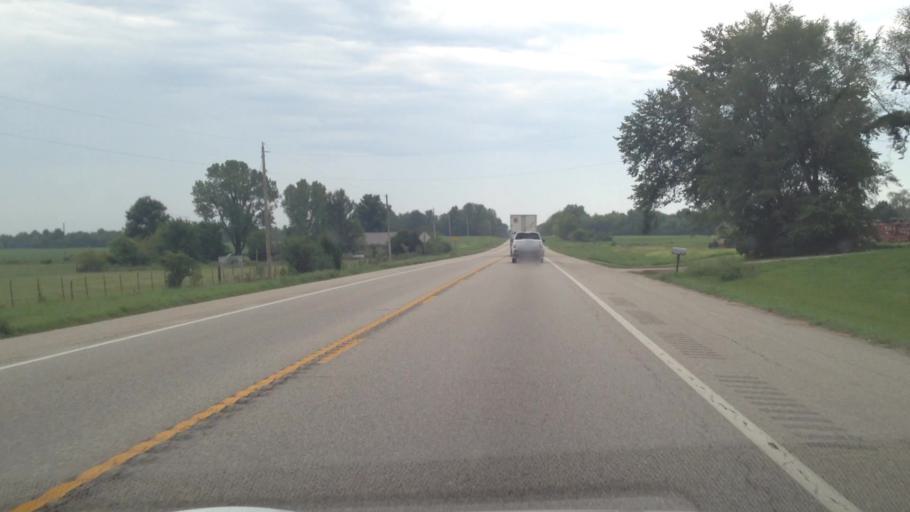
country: US
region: Kansas
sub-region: Crawford County
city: Pittsburg
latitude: 37.3265
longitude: -94.7054
